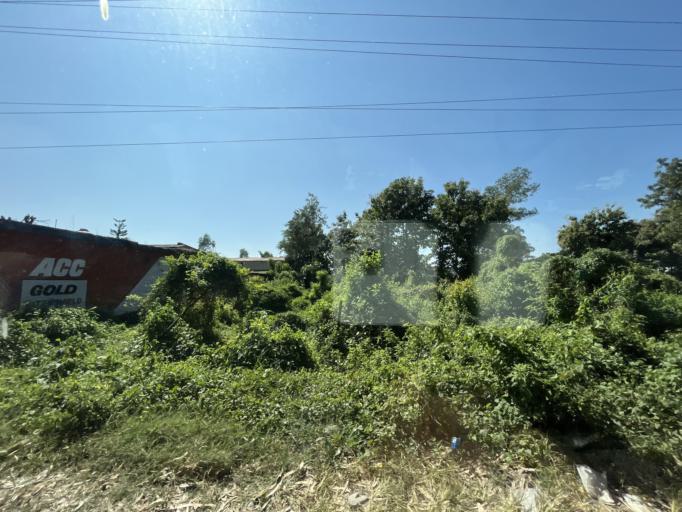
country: IN
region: Uttarakhand
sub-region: Naini Tal
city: Haldwani
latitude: 29.2110
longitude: 79.4622
